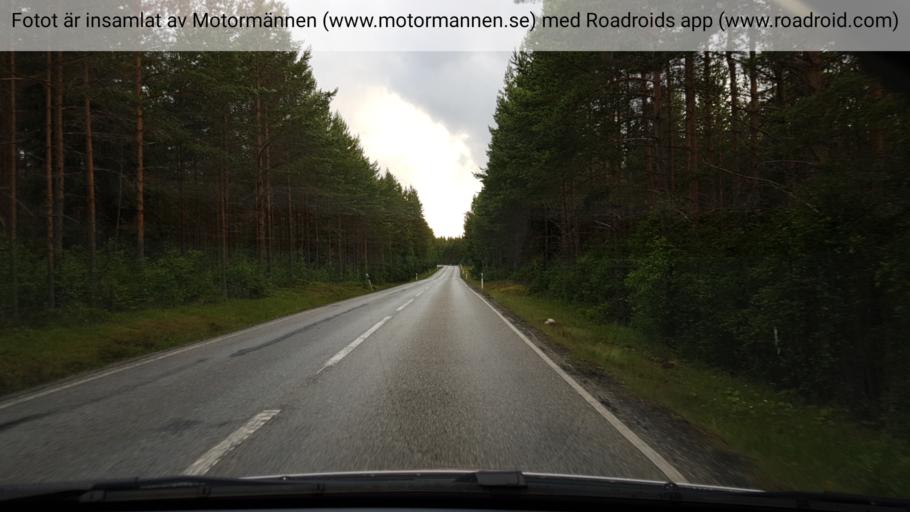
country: SE
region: OErebro
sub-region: Ljusnarsbergs Kommun
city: Kopparberg
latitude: 59.8096
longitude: 14.8999
